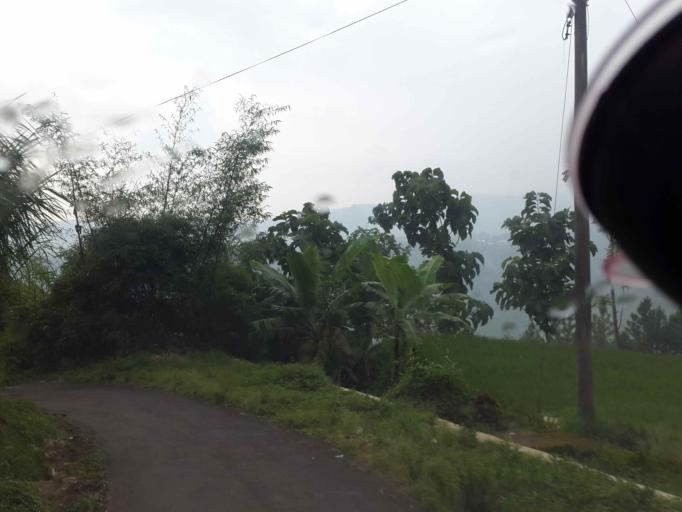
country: ID
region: Central Java
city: Lebaksiu
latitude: -7.1502
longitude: 109.1360
